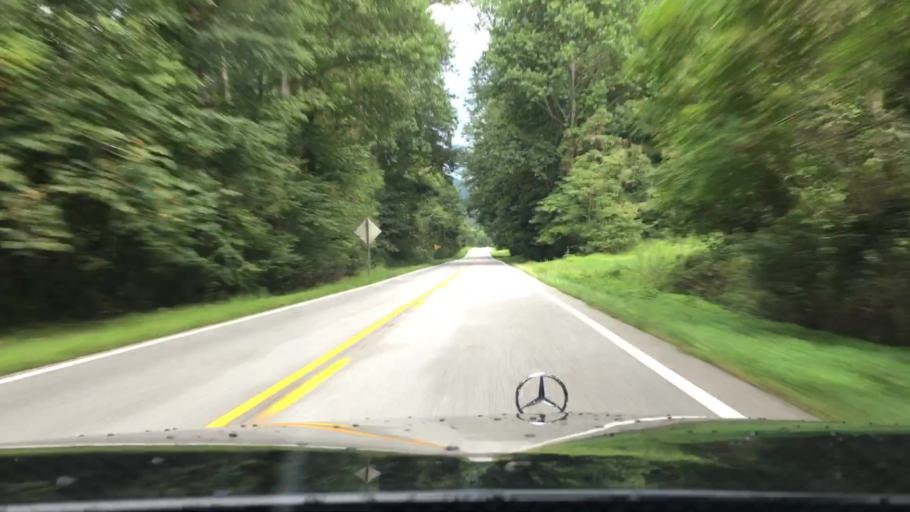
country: US
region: Virginia
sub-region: Nelson County
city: Nellysford
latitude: 37.8252
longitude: -78.9354
